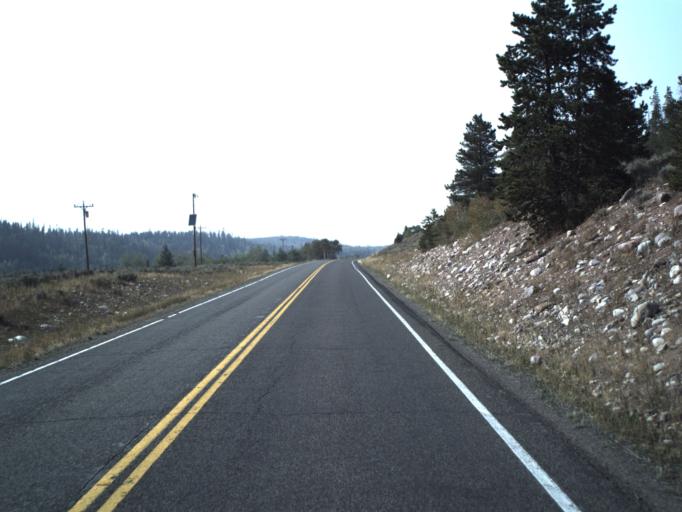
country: US
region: Wyoming
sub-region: Uinta County
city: Evanston
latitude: 40.9318
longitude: -110.8320
